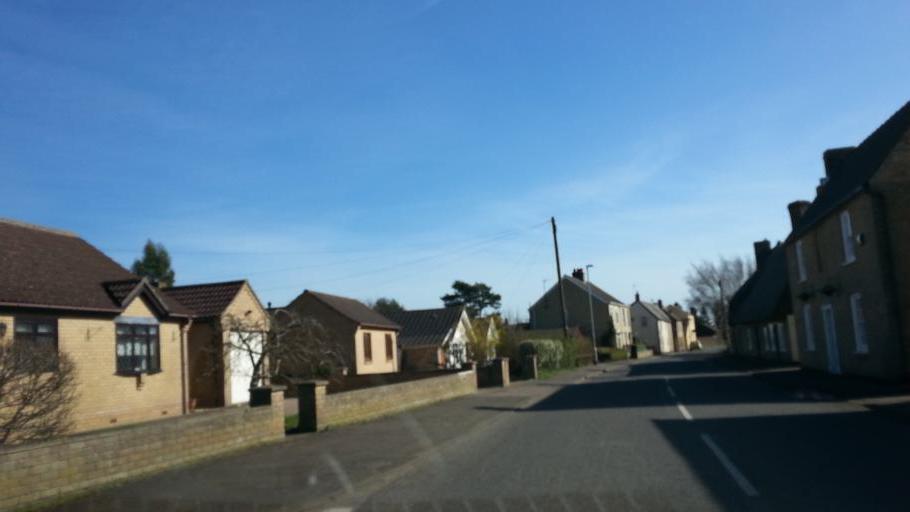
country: GB
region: England
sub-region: Cambridgeshire
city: Swavesey
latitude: 52.3102
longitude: 0.0164
